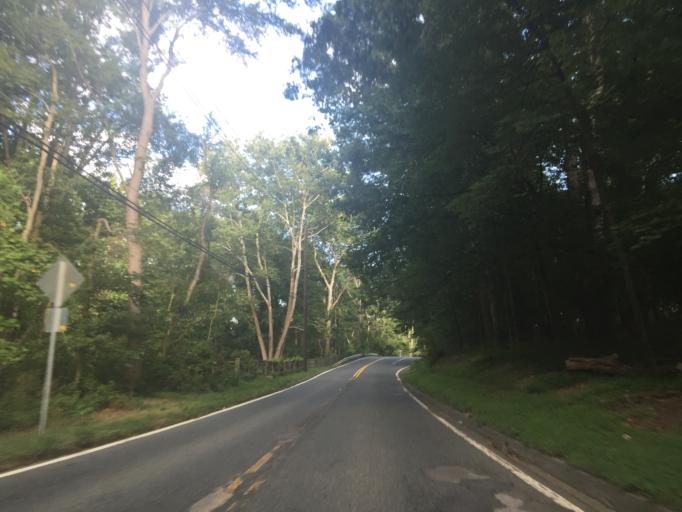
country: US
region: Maryland
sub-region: Montgomery County
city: Montgomery Village
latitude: 39.2051
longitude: -77.1648
